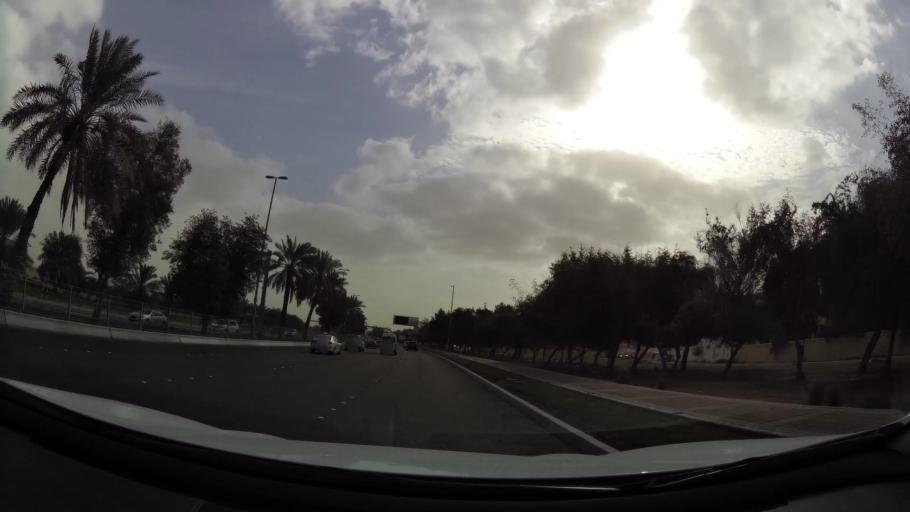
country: AE
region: Abu Dhabi
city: Abu Dhabi
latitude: 24.4162
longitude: 54.4678
